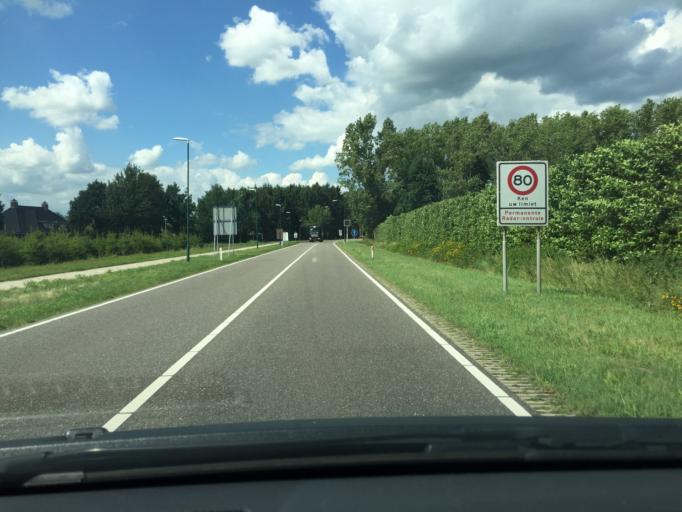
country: NL
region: North Brabant
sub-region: Gemeente Nuenen, Gerwen en Nederwetten
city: Nuenen
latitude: 51.4907
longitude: 5.5685
